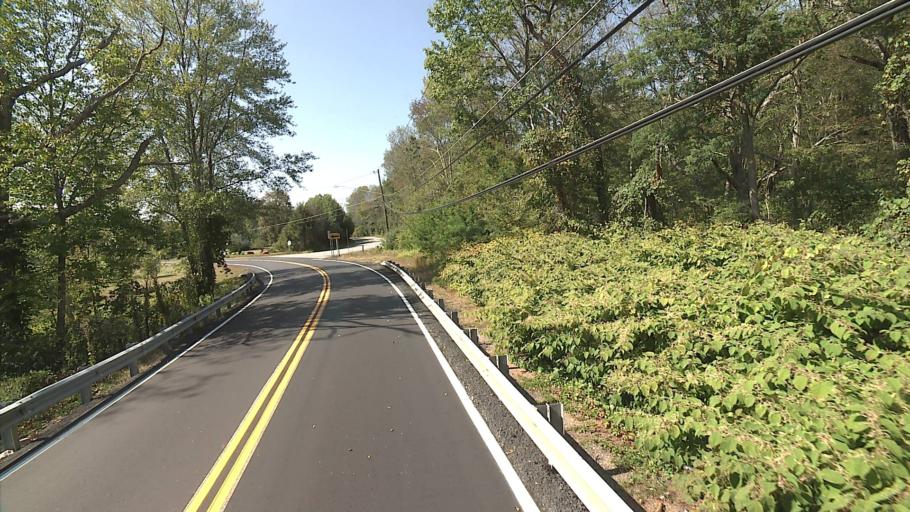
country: US
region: Connecticut
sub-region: Tolland County
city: Hebron
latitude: 41.7221
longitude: -72.4205
